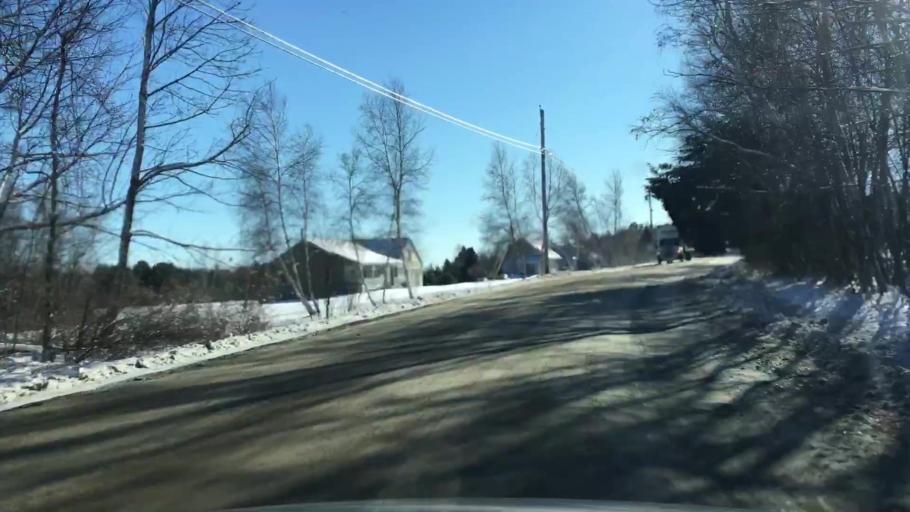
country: US
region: Maine
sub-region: Kennebec County
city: Winthrop
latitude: 44.3441
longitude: -69.9895
